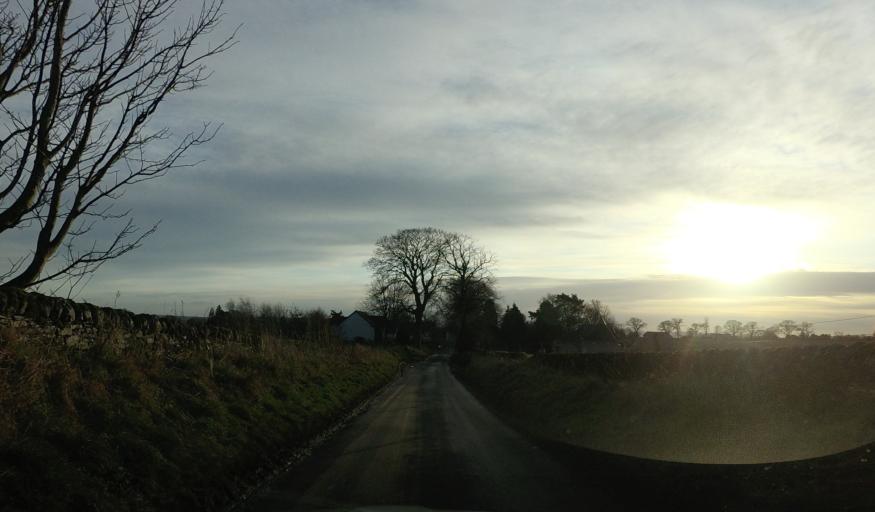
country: GB
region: Scotland
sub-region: Angus
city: Muirhead
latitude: 56.4910
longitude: -3.1032
